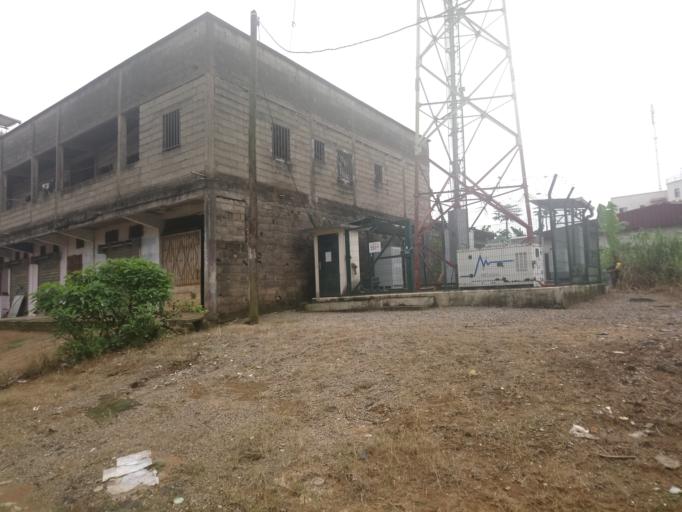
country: CM
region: Littoral
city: Douala
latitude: 4.0943
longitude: 9.7641
